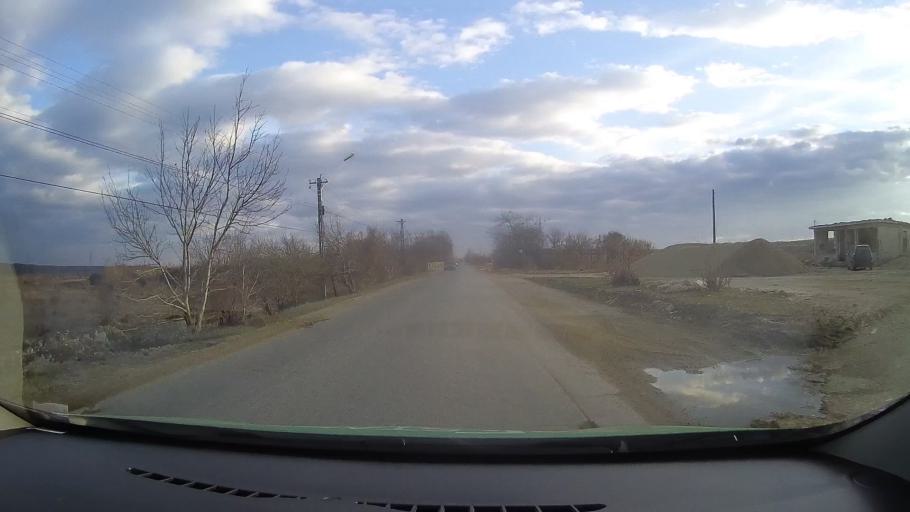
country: RO
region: Dambovita
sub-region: Comuna I. L. Caragiale
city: Ghirdoveni
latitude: 44.9597
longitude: 25.6573
